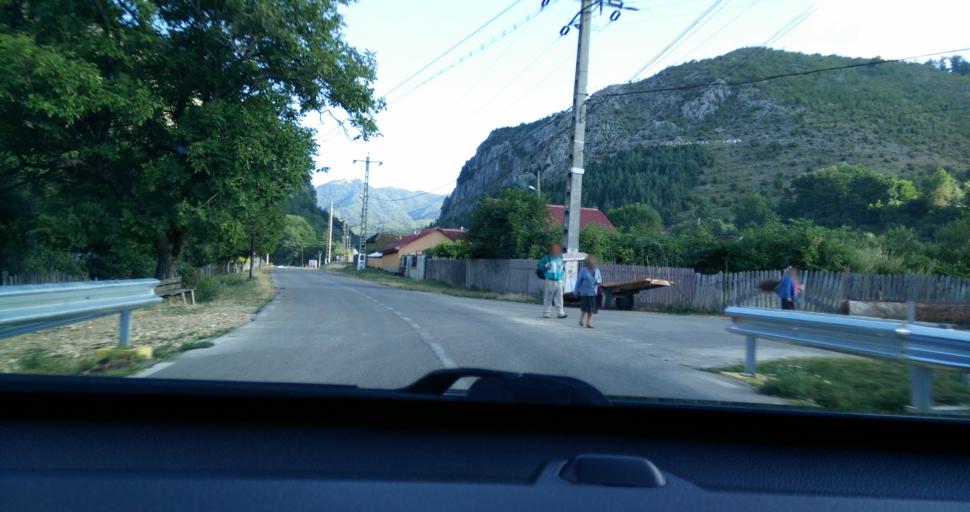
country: RO
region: Gorj
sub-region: Comuna Baia de Fier
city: Baia de Fier
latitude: 45.1841
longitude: 23.7578
